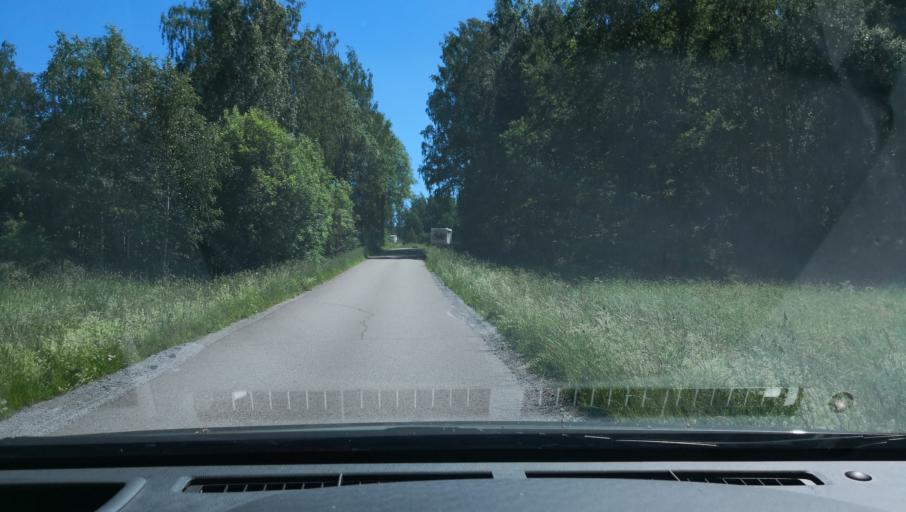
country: SE
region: Vaestmanland
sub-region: Arboga Kommun
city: Tyringe
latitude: 59.3852
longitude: 15.9451
